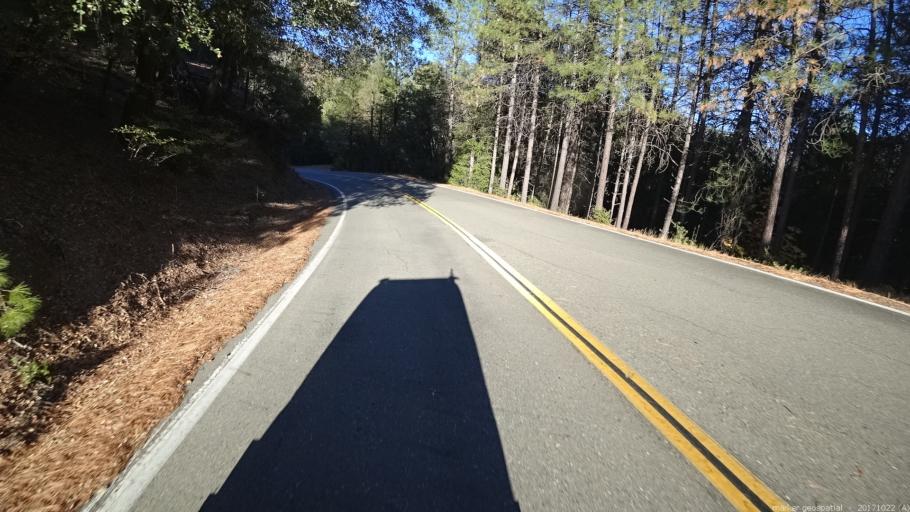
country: US
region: California
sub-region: Shasta County
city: Shasta Lake
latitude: 40.8735
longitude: -122.2481
